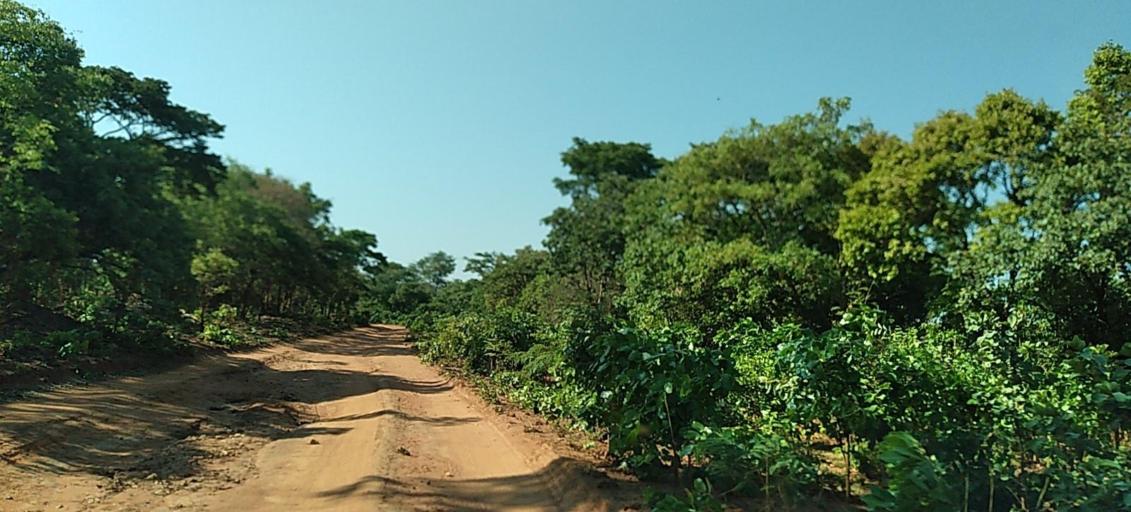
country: ZM
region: Central
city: Mkushi
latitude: -13.4683
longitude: 28.9163
